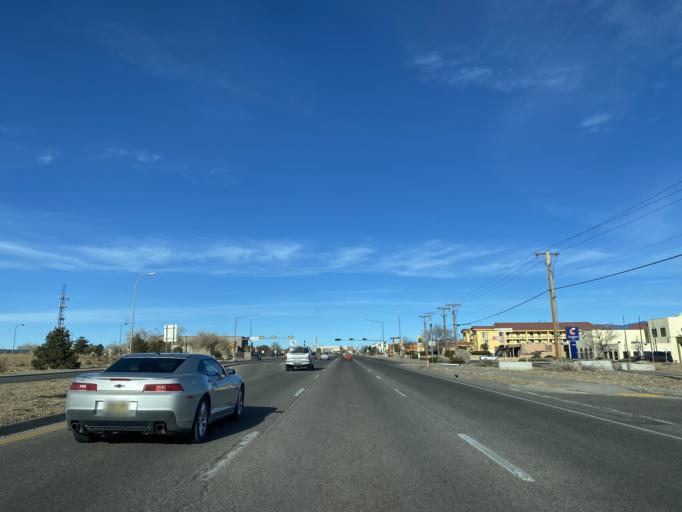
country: US
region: New Mexico
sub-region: Santa Fe County
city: Agua Fria
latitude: 35.6337
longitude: -106.0205
